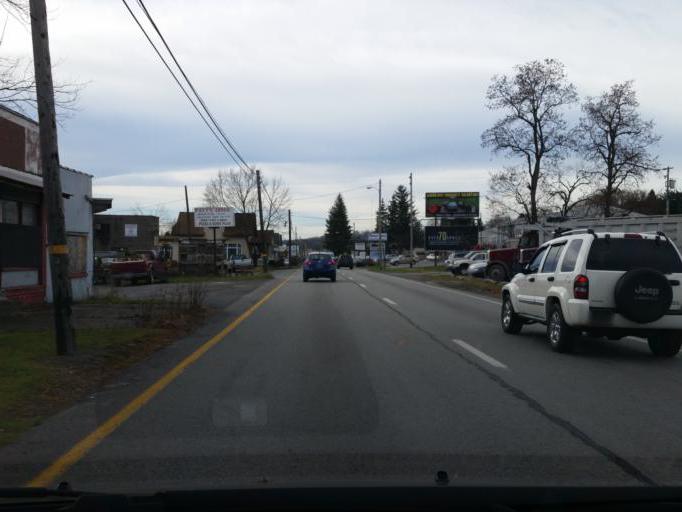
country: US
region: Pennsylvania
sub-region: Blair County
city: Altoona
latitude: 40.5093
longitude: -78.3833
